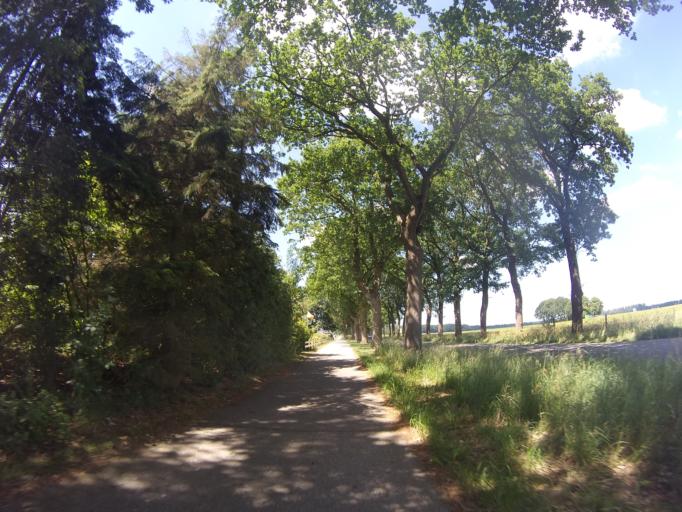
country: NL
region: Drenthe
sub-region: Gemeente Emmen
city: Emmen
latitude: 52.8457
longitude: 6.8677
